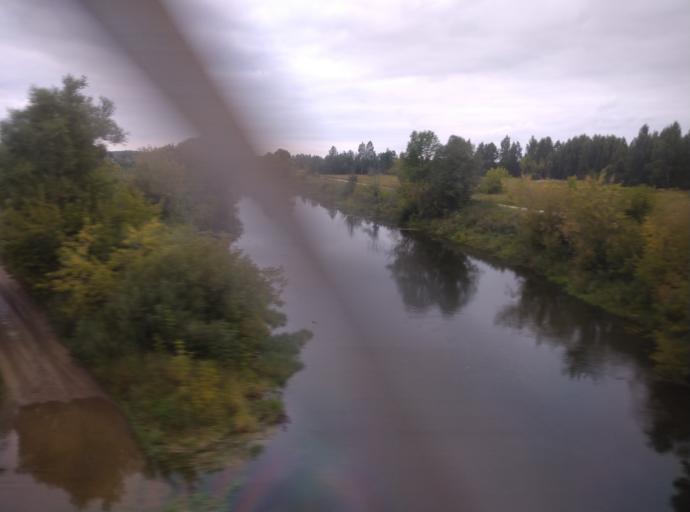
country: RU
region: Kostroma
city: Nerekhta
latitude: 57.4769
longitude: 40.5828
